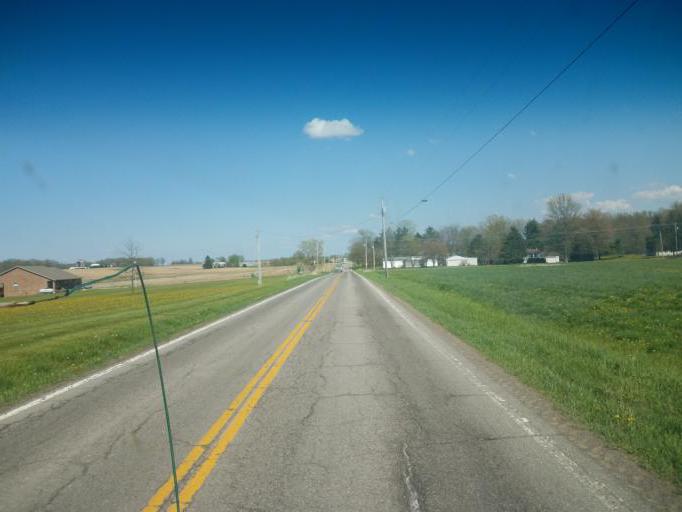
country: US
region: Ohio
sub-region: Wayne County
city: West Salem
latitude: 40.9220
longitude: -82.0834
